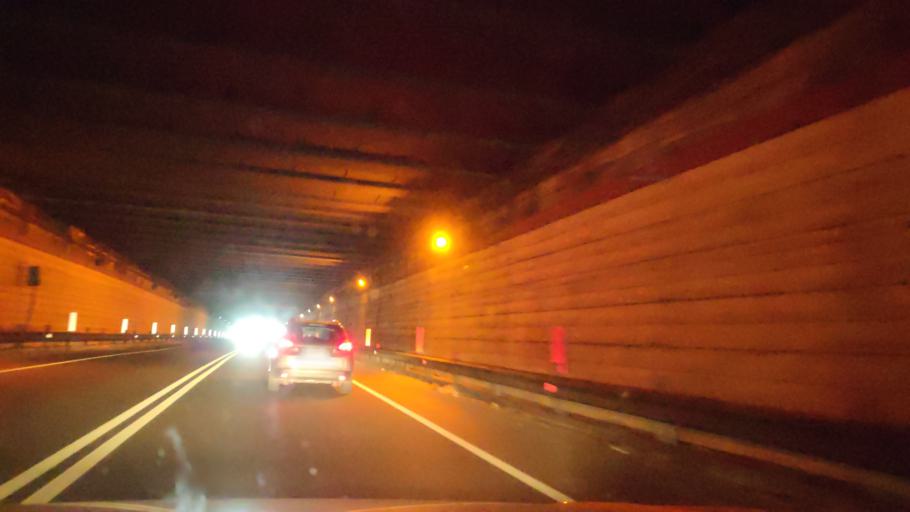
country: IT
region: Calabria
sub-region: Provincia di Catanzaro
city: Soverato Superiore
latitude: 38.6929
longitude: 16.5396
